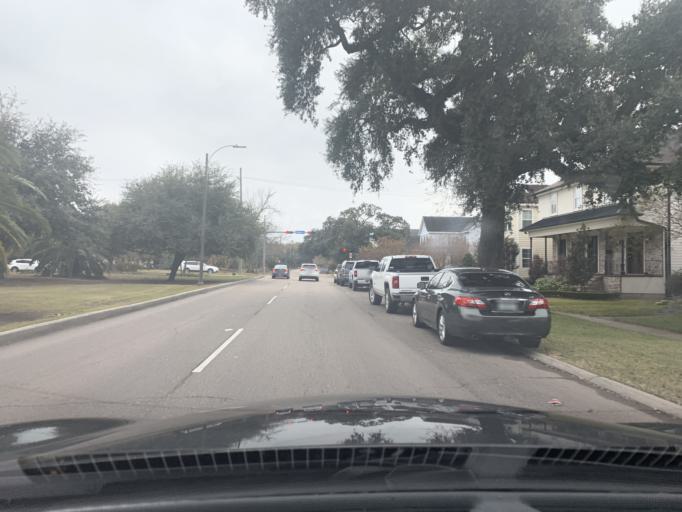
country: US
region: Louisiana
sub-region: Jefferson Parish
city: Metairie
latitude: 30.0129
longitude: -90.1073
